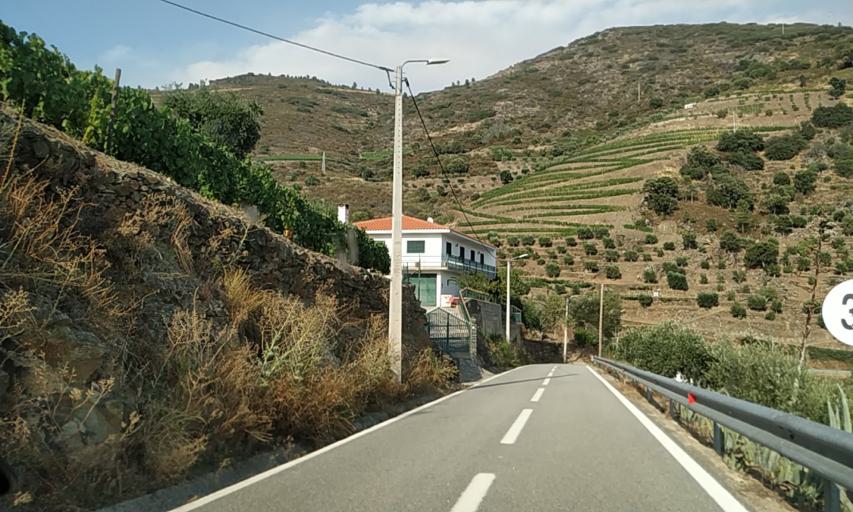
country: PT
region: Viseu
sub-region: Tabuaco
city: Tabuaco
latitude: 41.1363
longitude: -7.5354
